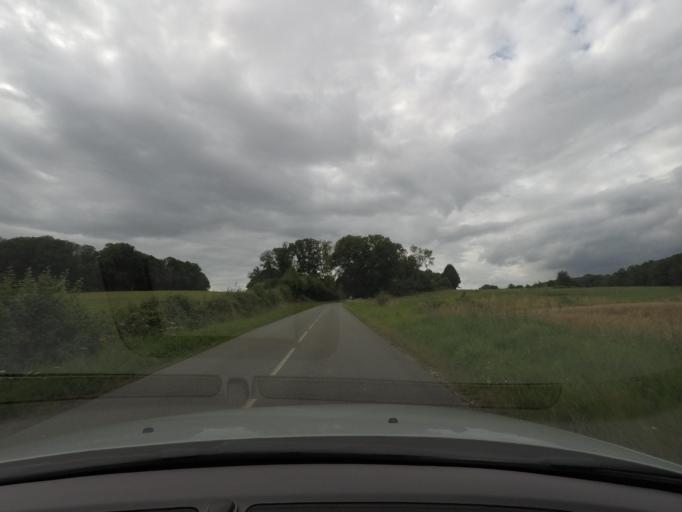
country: FR
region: Haute-Normandie
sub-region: Departement de l'Eure
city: Les Andelys
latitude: 49.2828
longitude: 1.3491
